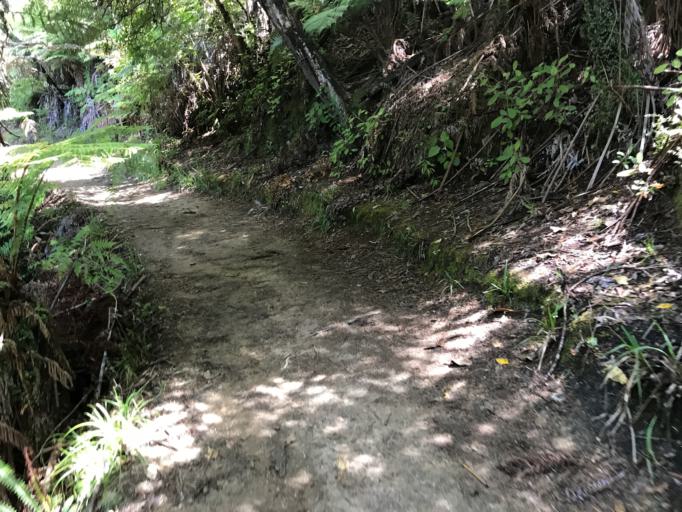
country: NZ
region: Marlborough
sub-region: Marlborough District
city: Picton
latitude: -41.2575
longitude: 173.9375
